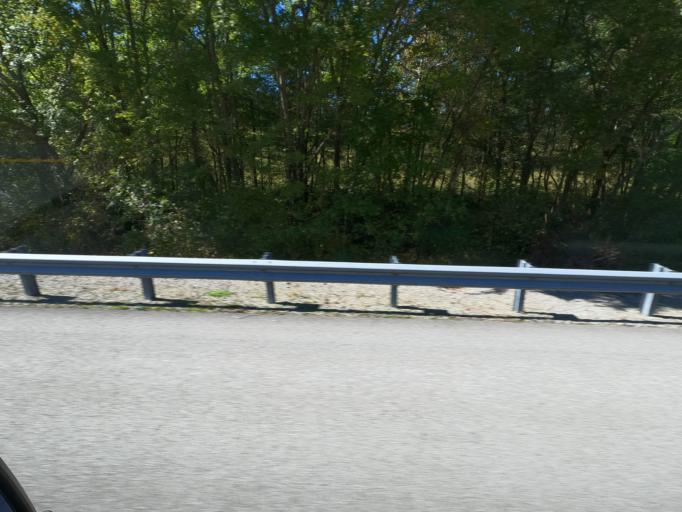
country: US
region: Tennessee
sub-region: Maury County
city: Mount Pleasant
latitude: 35.4147
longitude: -87.2821
